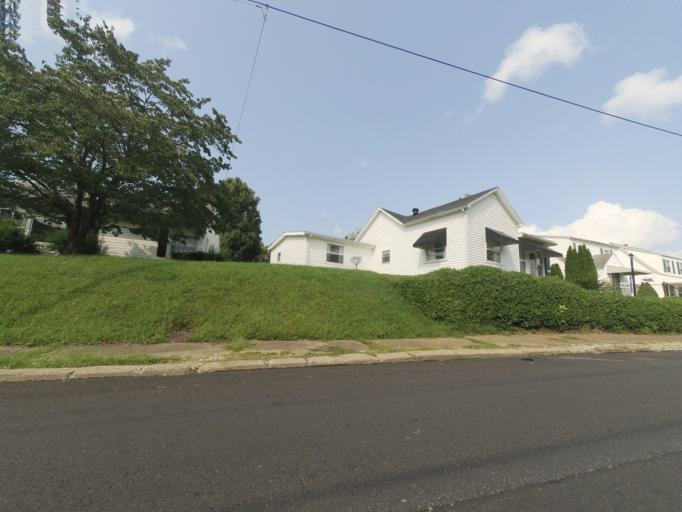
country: US
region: West Virginia
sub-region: Cabell County
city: Huntington
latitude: 38.4047
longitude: -82.4020
